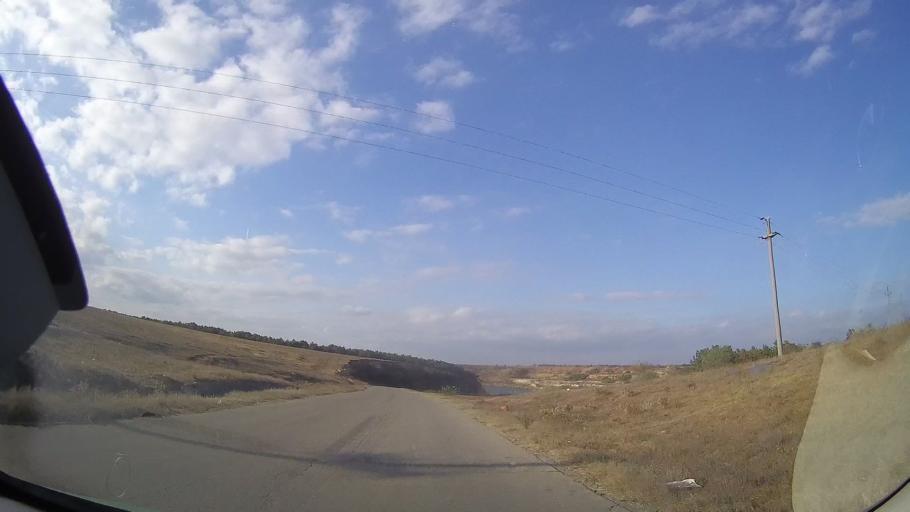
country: RO
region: Constanta
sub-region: Comuna Limanu
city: Limanu
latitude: 43.8097
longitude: 28.5192
